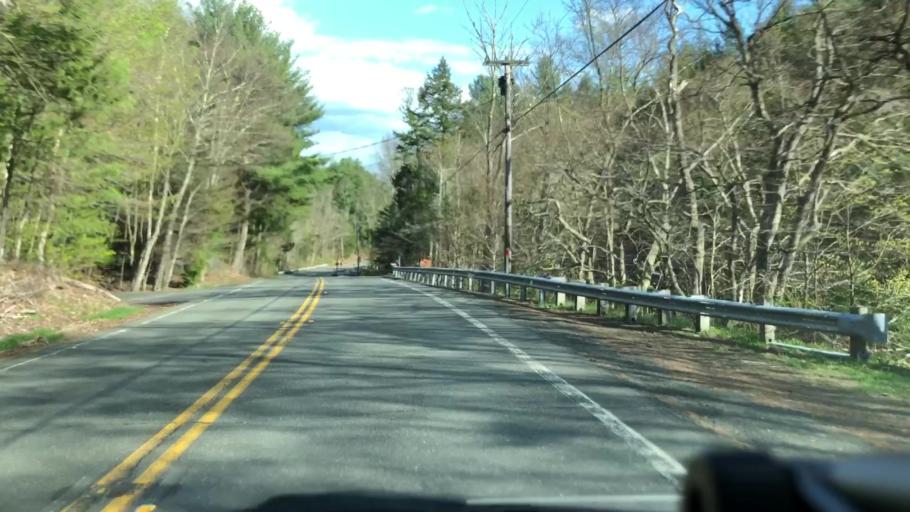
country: US
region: Massachusetts
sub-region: Hampshire County
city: Chesterfield
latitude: 42.3514
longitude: -72.9041
